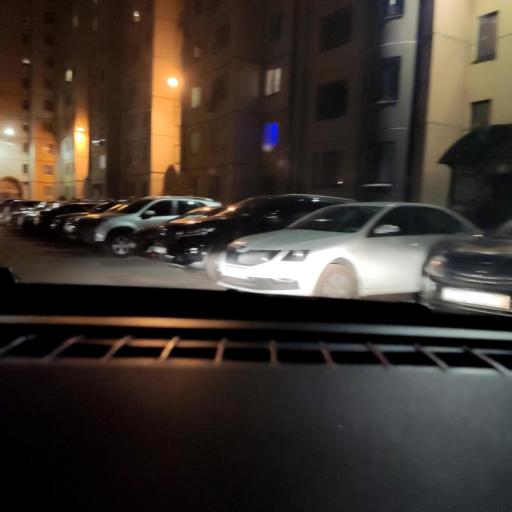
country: RU
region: Voronezj
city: Voronezh
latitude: 51.6483
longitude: 39.2341
